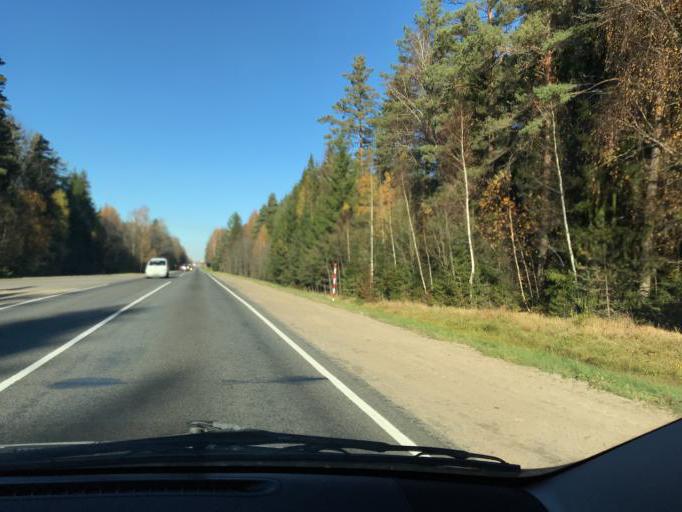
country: BY
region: Vitebsk
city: Polatsk
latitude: 55.4389
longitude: 28.7776
